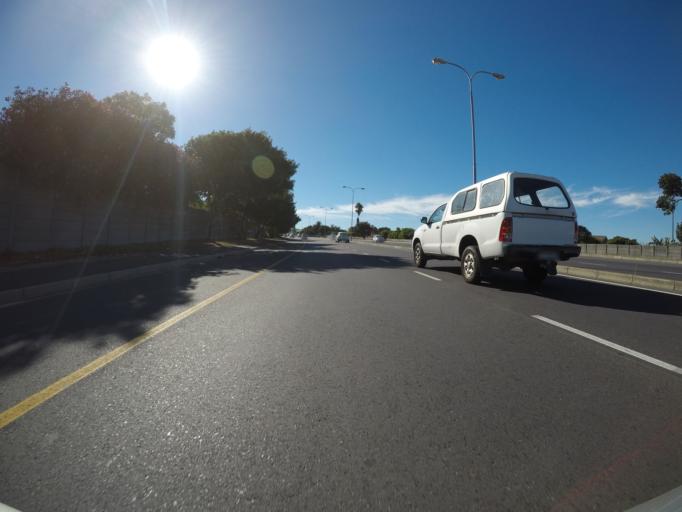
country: ZA
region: Western Cape
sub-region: City of Cape Town
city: Kraaifontein
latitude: -33.8851
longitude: 18.6697
